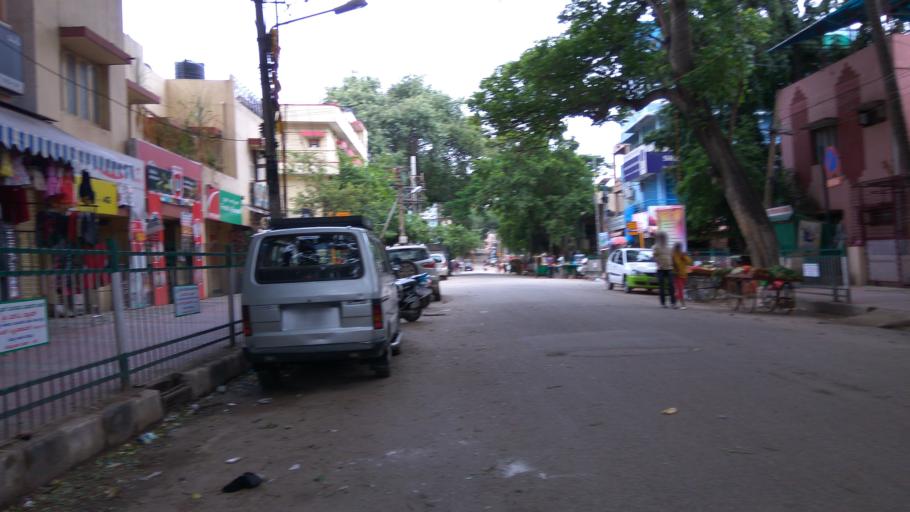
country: IN
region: Karnataka
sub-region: Bangalore Urban
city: Bangalore
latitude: 12.9588
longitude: 77.6384
